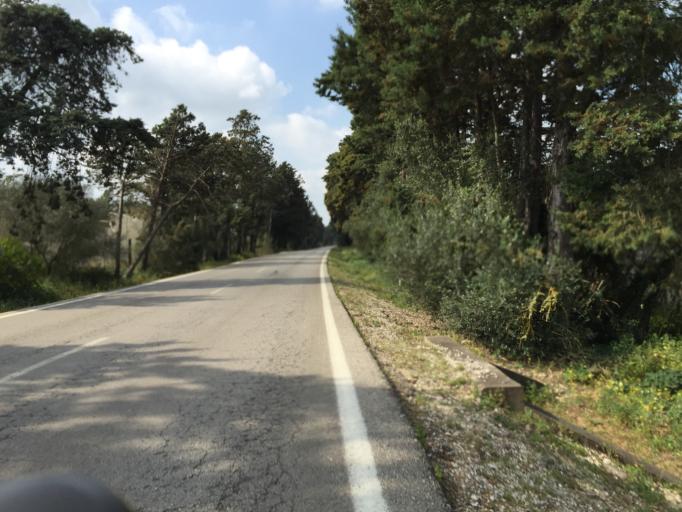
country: ES
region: Andalusia
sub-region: Provincia de Cadiz
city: Benalup-Casas Viejas
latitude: 36.3068
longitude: -5.8966
